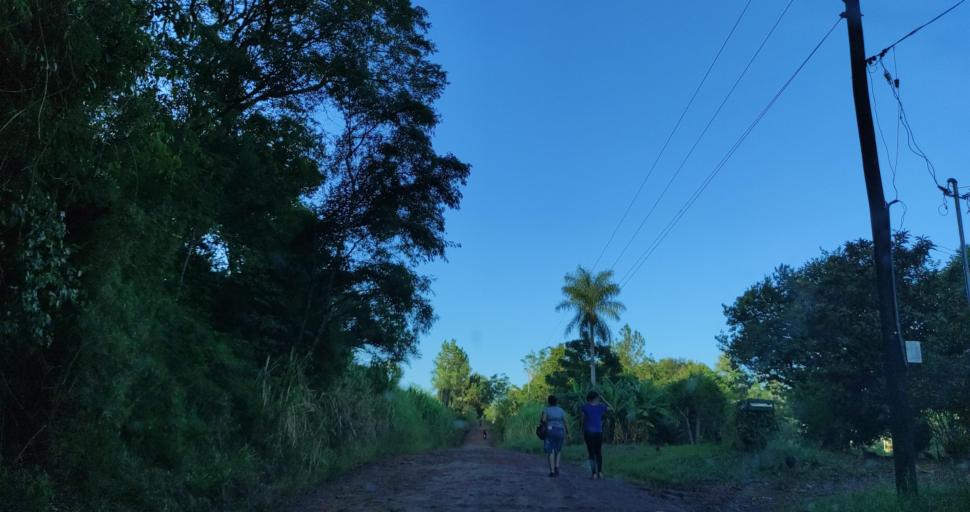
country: AR
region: Misiones
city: Gobernador Roca
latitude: -27.2186
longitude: -55.4248
